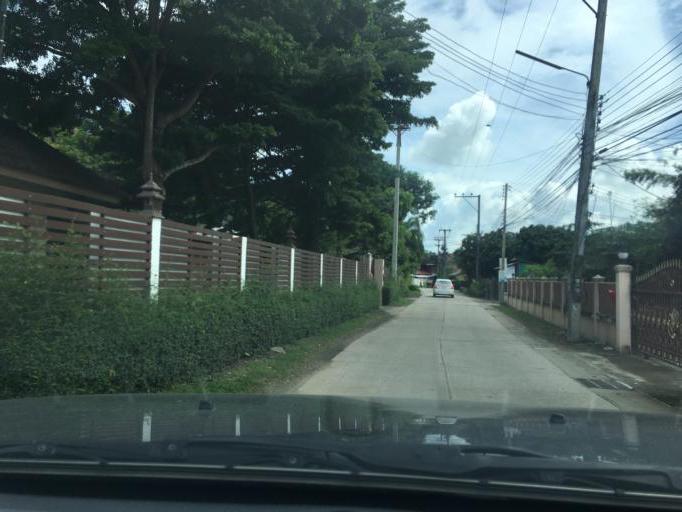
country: TH
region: Chiang Mai
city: San Sai
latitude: 18.8776
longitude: 98.9699
